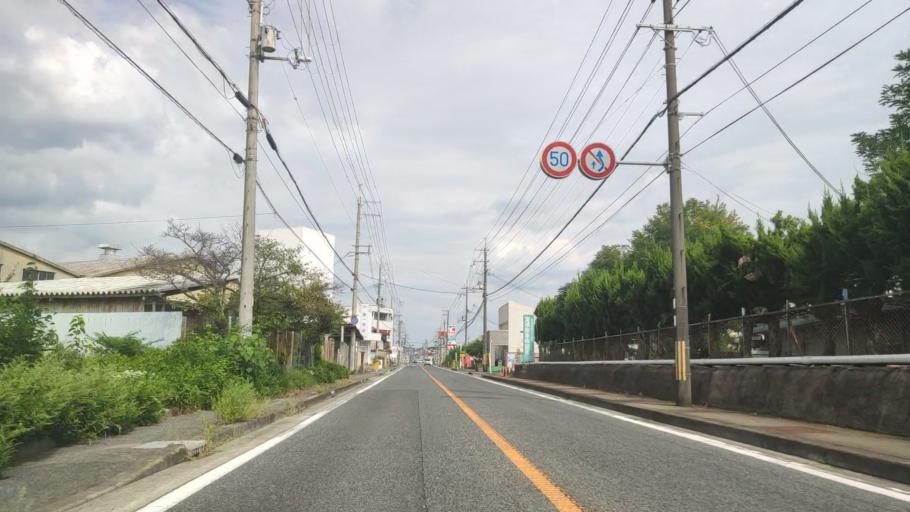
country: JP
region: Wakayama
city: Hashimoto
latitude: 34.3046
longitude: 135.5674
